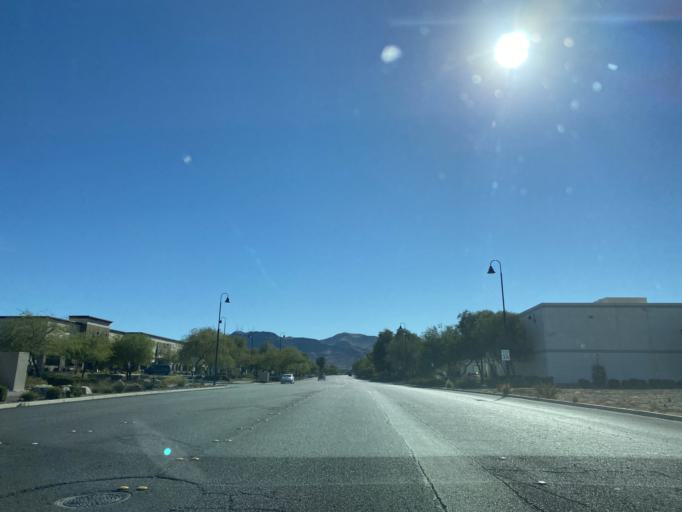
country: US
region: Nevada
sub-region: Clark County
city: Henderson
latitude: 36.0558
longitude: -115.0200
